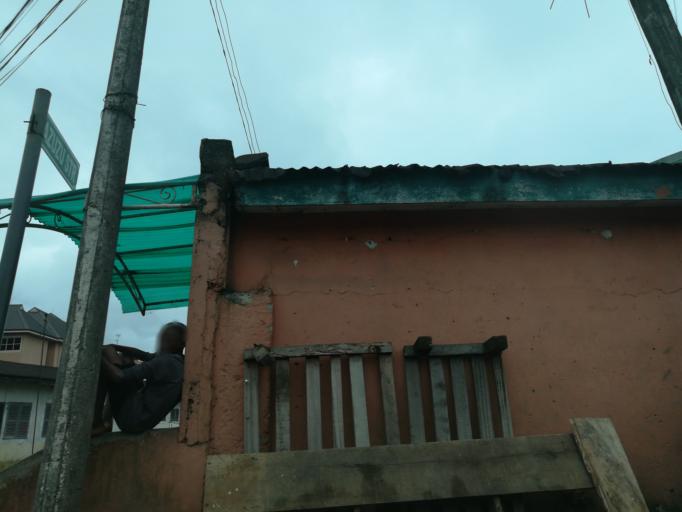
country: NG
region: Rivers
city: Port Harcourt
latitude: 4.8281
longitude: 7.0242
